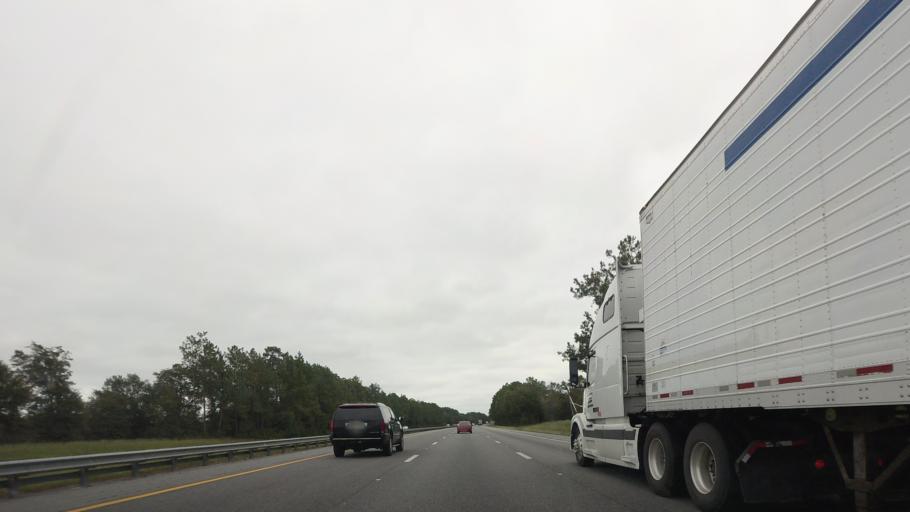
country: US
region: Florida
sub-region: Hamilton County
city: Jasper
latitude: 30.5658
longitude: -83.0916
